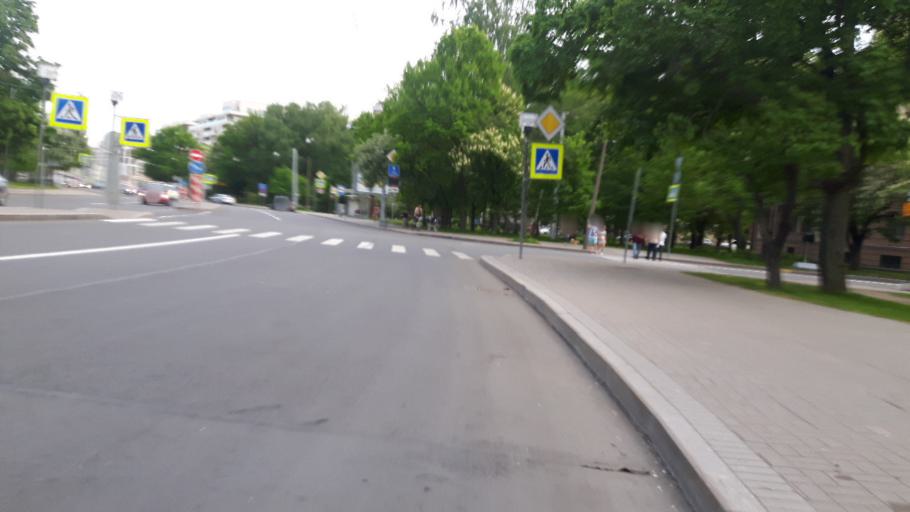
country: RU
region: Leningrad
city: Krestovskiy ostrov
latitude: 59.9704
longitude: 30.2751
